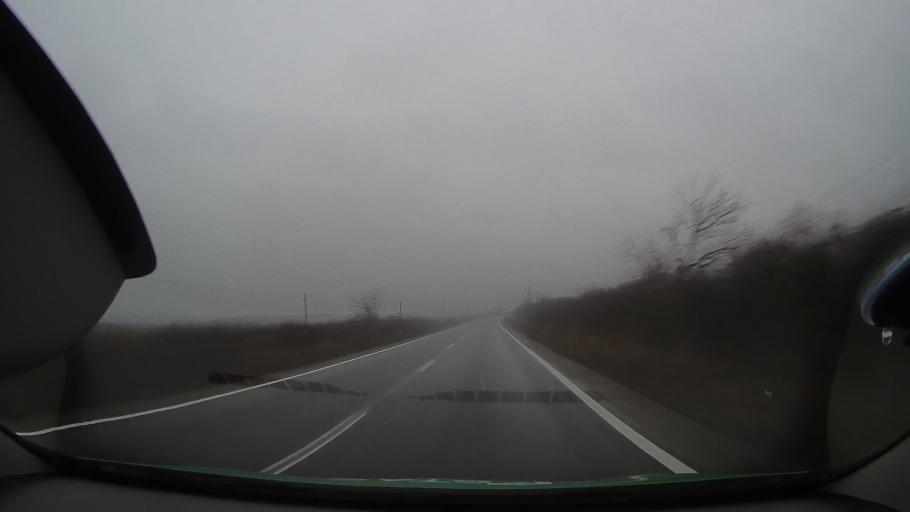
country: RO
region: Bihor
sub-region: Comuna Olcea
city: Calacea
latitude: 46.7250
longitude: 21.9460
